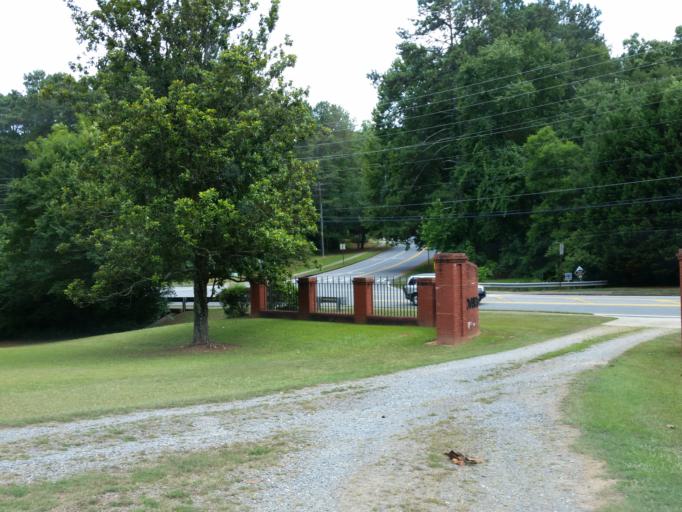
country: US
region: Georgia
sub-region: Cherokee County
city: Woodstock
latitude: 34.0516
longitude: -84.5069
